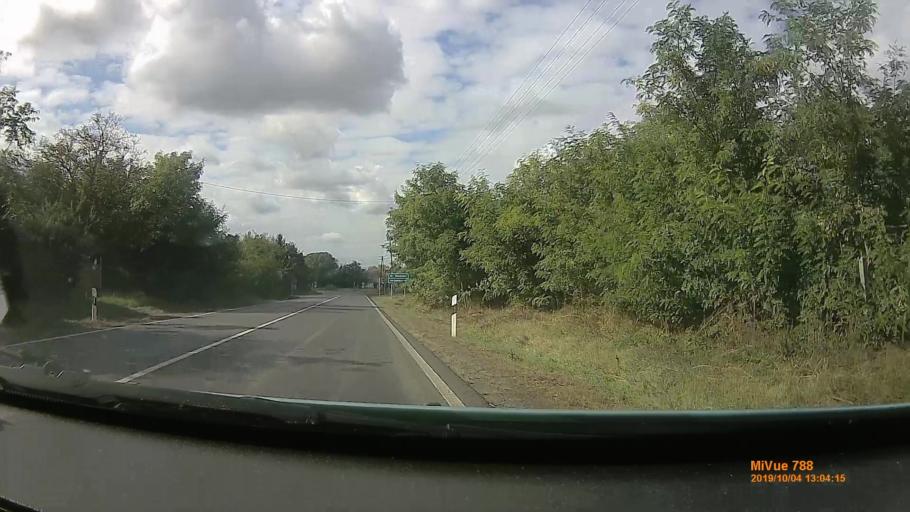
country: HU
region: Szabolcs-Szatmar-Bereg
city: Nyirtelek
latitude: 47.9586
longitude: 21.6303
